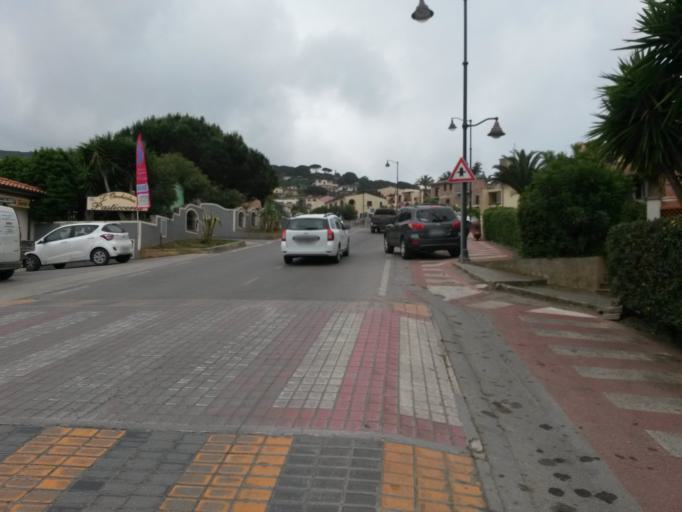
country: IT
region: Tuscany
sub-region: Provincia di Livorno
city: Capoliveri
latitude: 42.7455
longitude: 10.3814
